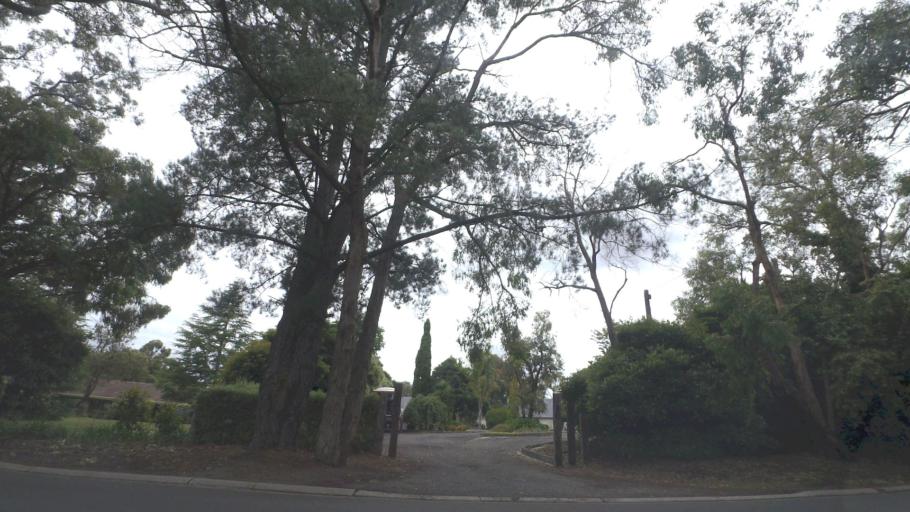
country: AU
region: Victoria
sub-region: Manningham
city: Park Orchards
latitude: -37.7857
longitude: 145.2269
